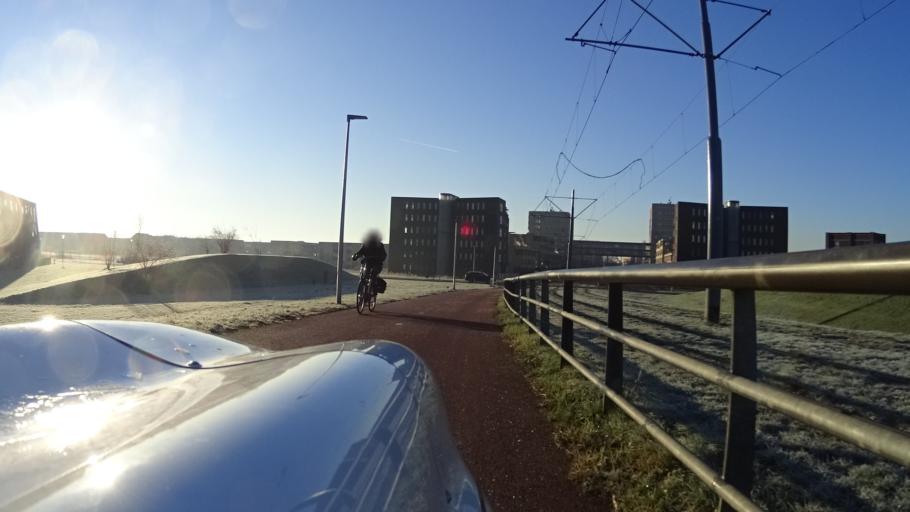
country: NL
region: South Holland
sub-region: Gemeente Barendrecht
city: Barendrecht
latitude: 51.8633
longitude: 4.5038
